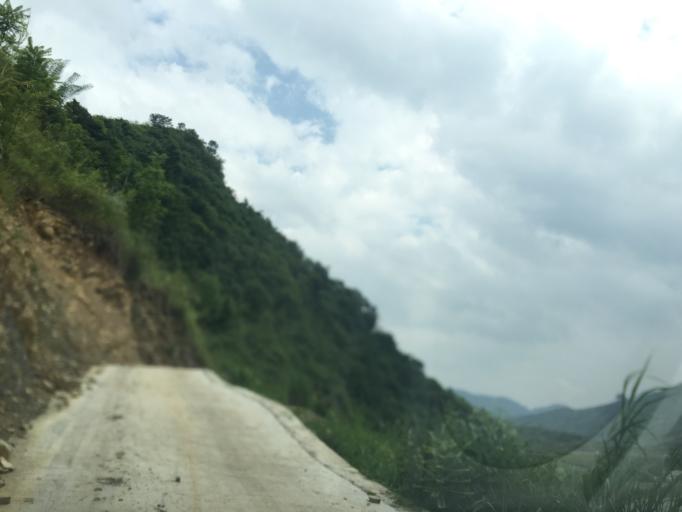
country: CN
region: Guangxi Zhuangzu Zizhiqu
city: Xinzhou
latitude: 25.1923
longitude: 105.7317
